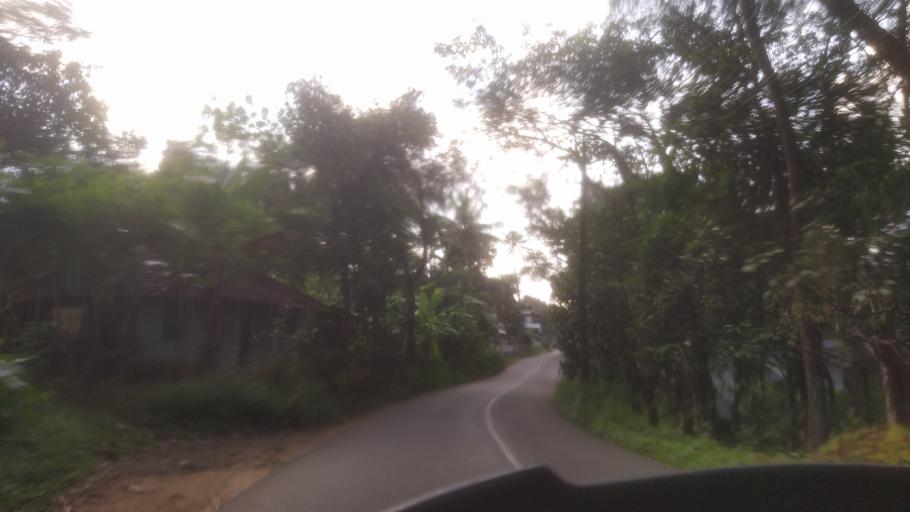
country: IN
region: Kerala
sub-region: Ernakulam
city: Kotamangalam
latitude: 10.0066
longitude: 76.6754
